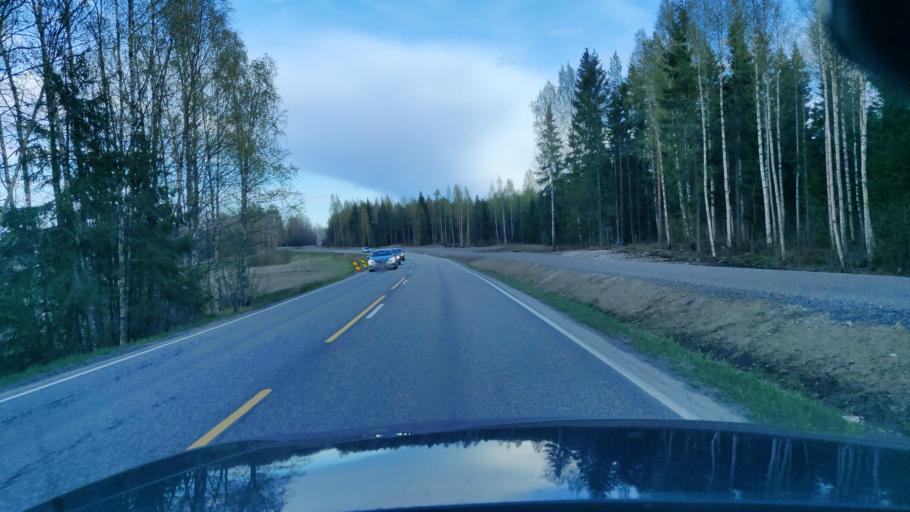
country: FI
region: Uusimaa
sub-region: Helsinki
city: Jaervenpaeae
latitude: 60.4805
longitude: 25.0588
